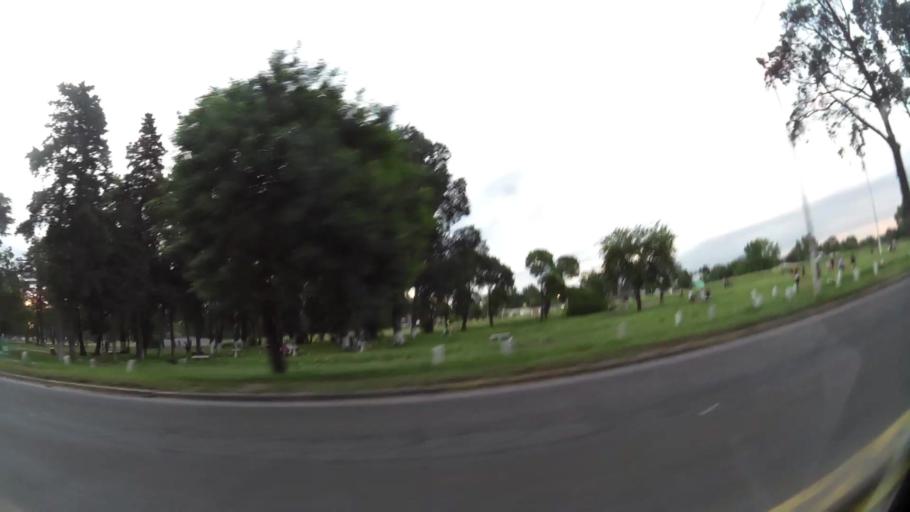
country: AR
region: Buenos Aires
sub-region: Partido de Merlo
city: Merlo
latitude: -34.6838
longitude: -58.7619
